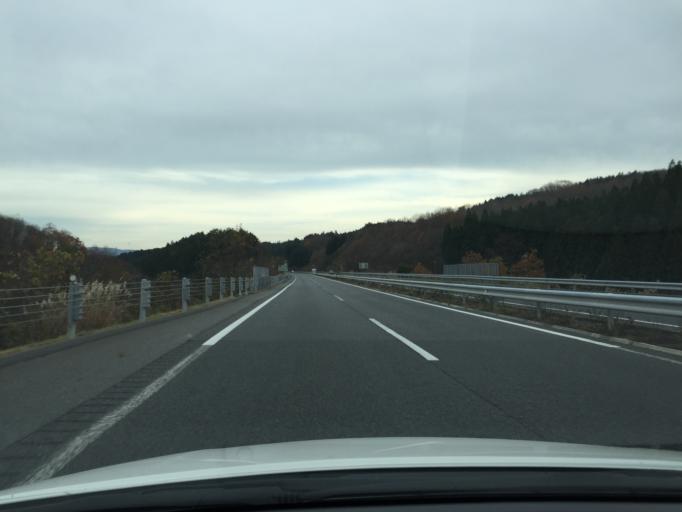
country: JP
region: Fukushima
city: Iwaki
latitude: 37.1897
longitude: 140.7079
